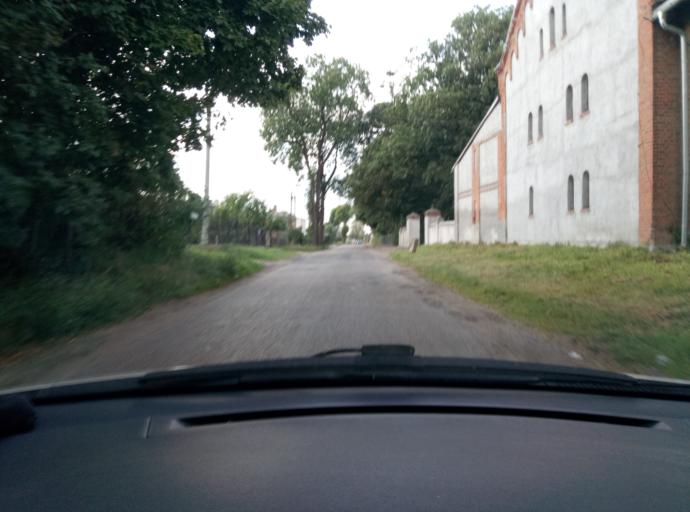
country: PL
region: Kujawsko-Pomorskie
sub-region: Powiat brodnicki
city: Jablonowo Pomorskie
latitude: 53.3860
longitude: 19.1711
